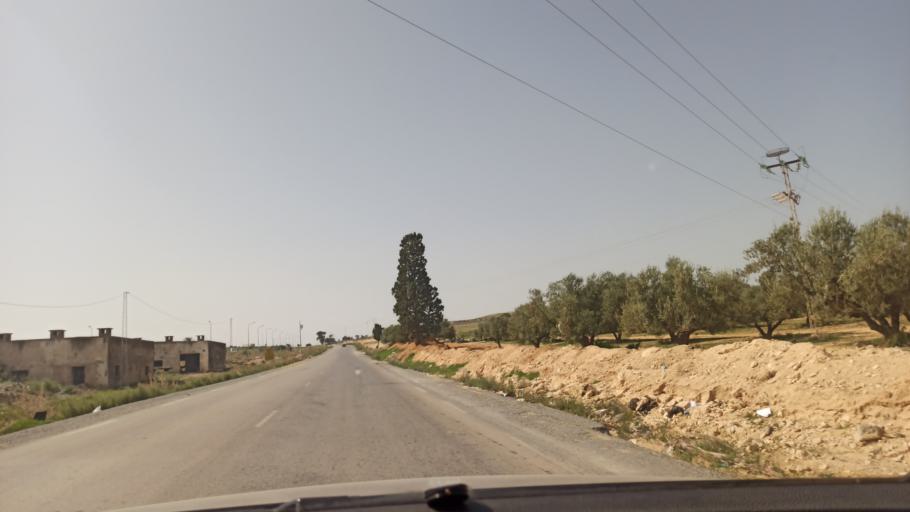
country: TN
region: Manouba
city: Manouba
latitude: 36.7416
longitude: 10.0889
